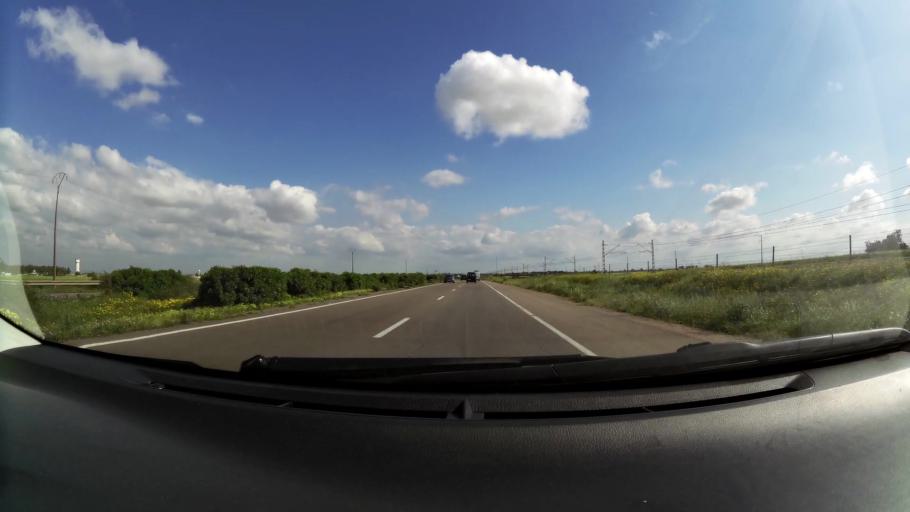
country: MA
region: Chaouia-Ouardigha
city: Nouaseur
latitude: 33.3515
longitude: -7.6162
